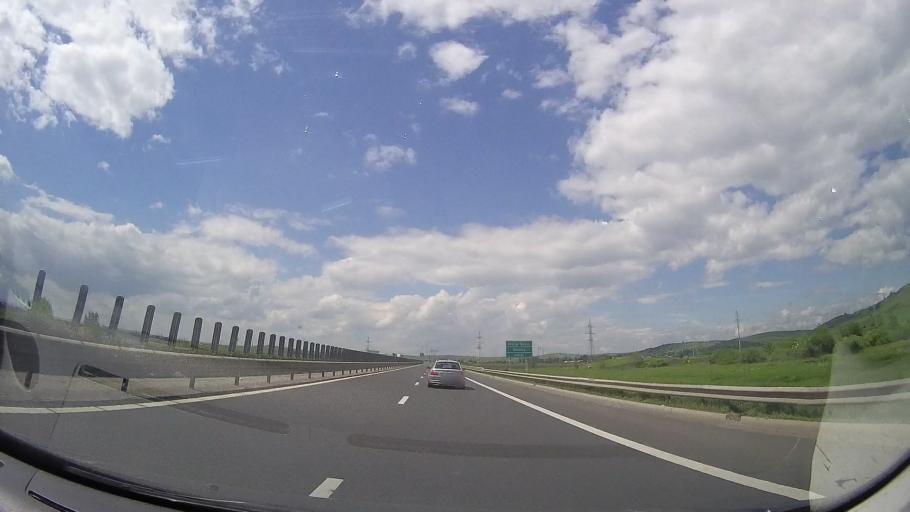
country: RO
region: Sibiu
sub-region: Municipiul Sibiu
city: Sibiu
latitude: 45.8154
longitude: 24.1665
